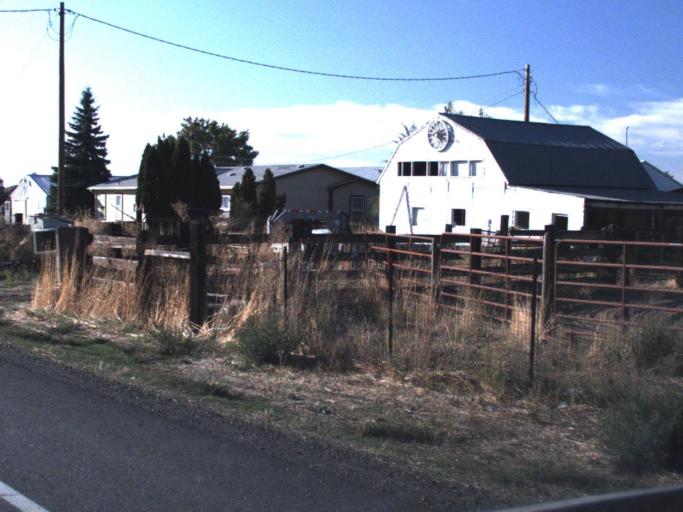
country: US
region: Washington
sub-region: Walla Walla County
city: Burbank
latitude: 46.2117
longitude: -118.9937
